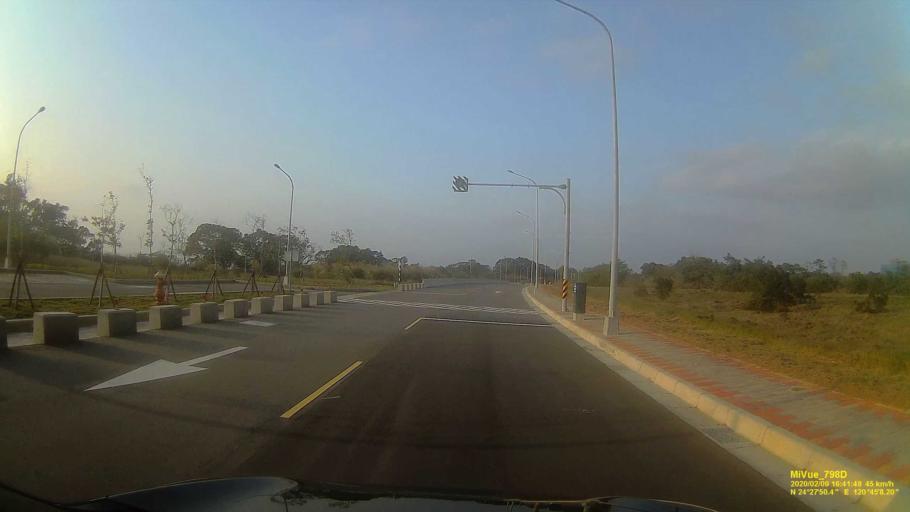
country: TW
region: Taiwan
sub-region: Miaoli
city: Miaoli
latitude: 24.4641
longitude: 120.7523
